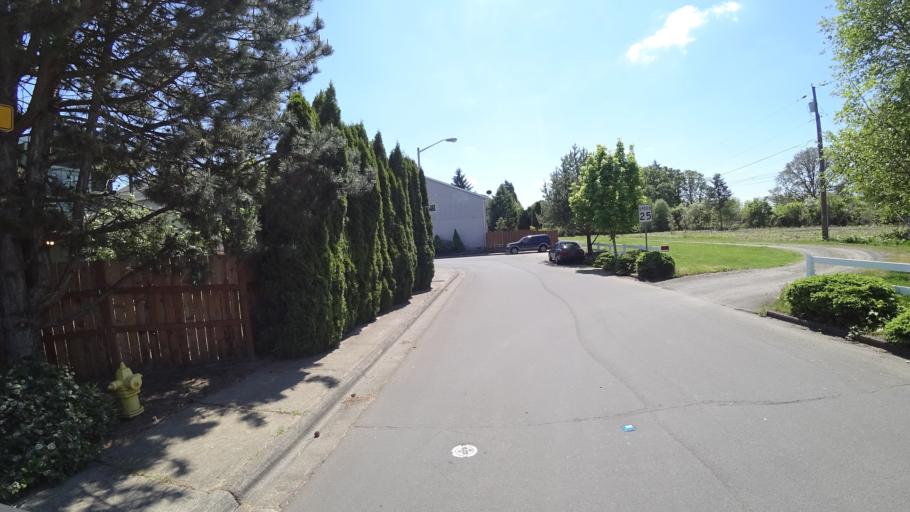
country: US
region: Oregon
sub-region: Washington County
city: Aloha
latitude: 45.5151
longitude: -122.8955
